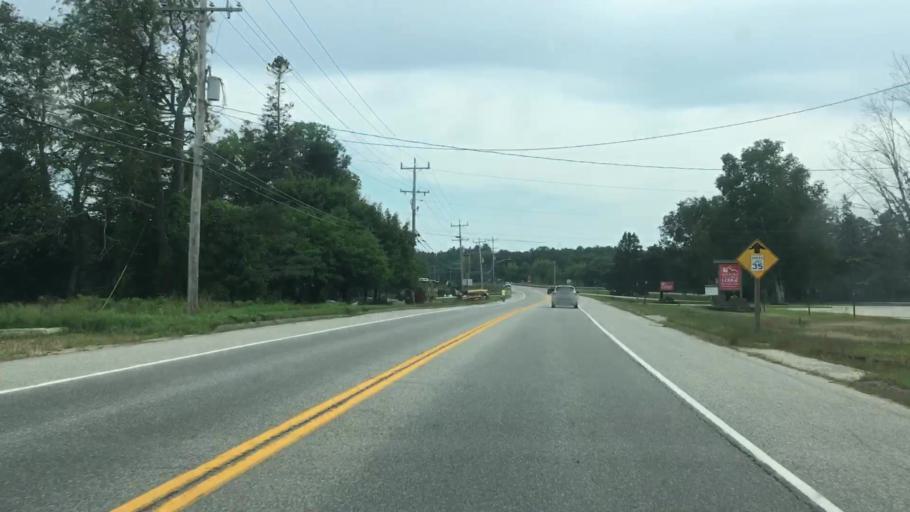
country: US
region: Maine
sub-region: Oxford County
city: Bethel
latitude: 44.4203
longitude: -70.7974
